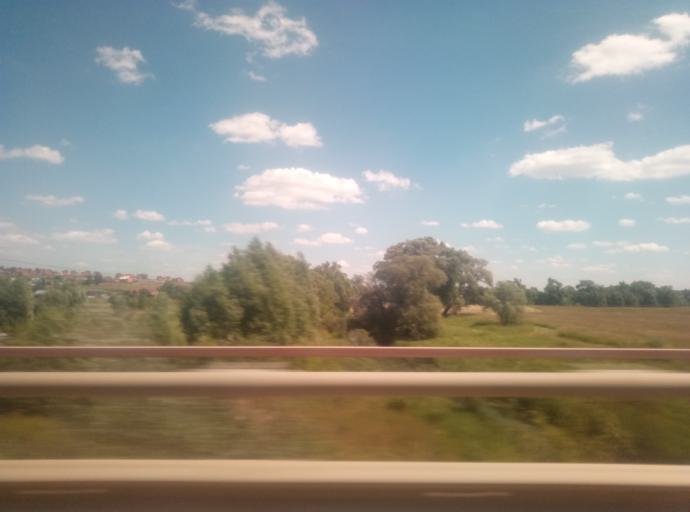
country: RU
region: Tula
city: Kireyevsk
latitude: 53.9735
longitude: 37.9299
